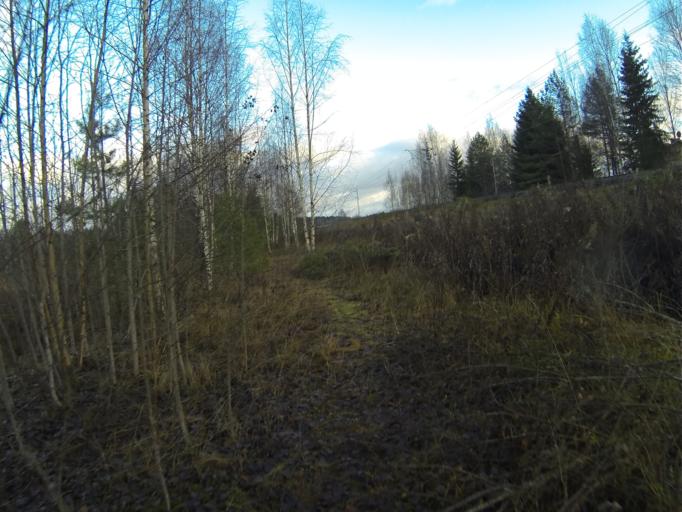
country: FI
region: Varsinais-Suomi
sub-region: Salo
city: Halikko
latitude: 60.3959
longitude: 23.0670
